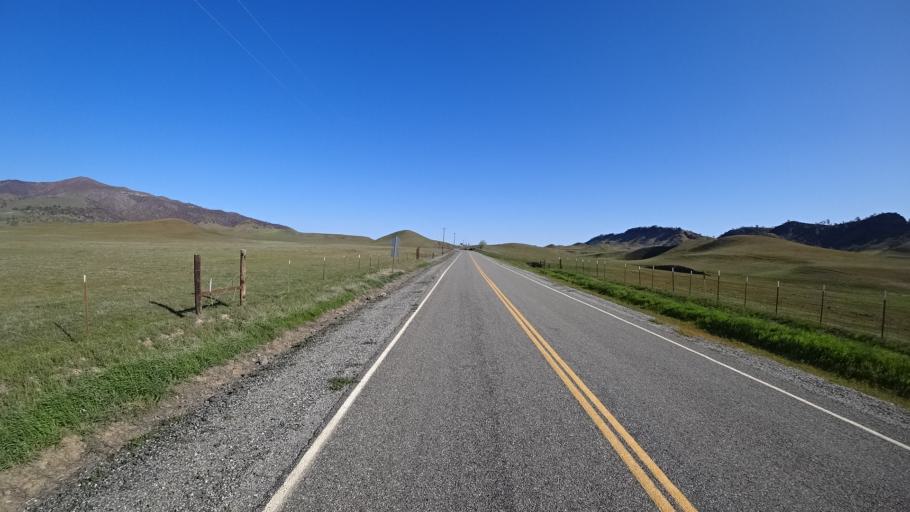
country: US
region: California
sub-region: Tehama County
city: Rancho Tehama Reserve
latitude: 39.7039
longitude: -122.5505
